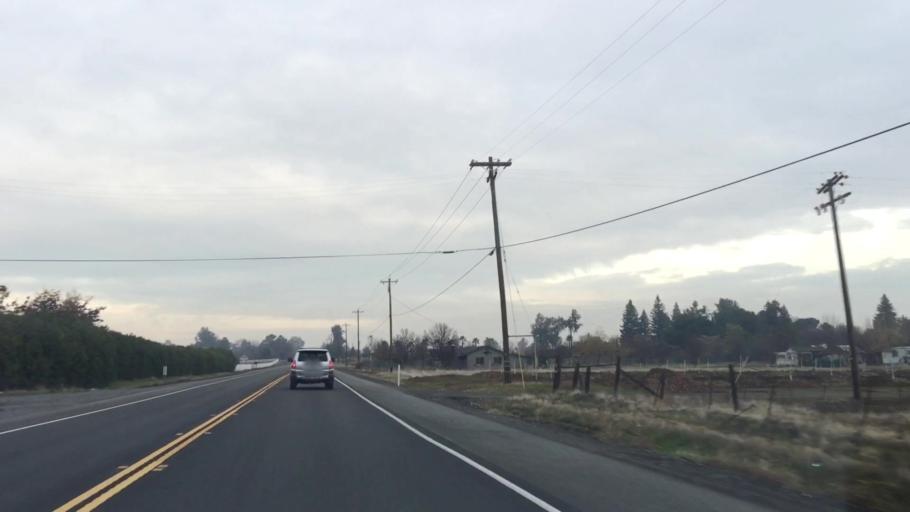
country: US
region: California
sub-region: Butte County
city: Palermo
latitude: 39.3971
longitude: -121.6048
